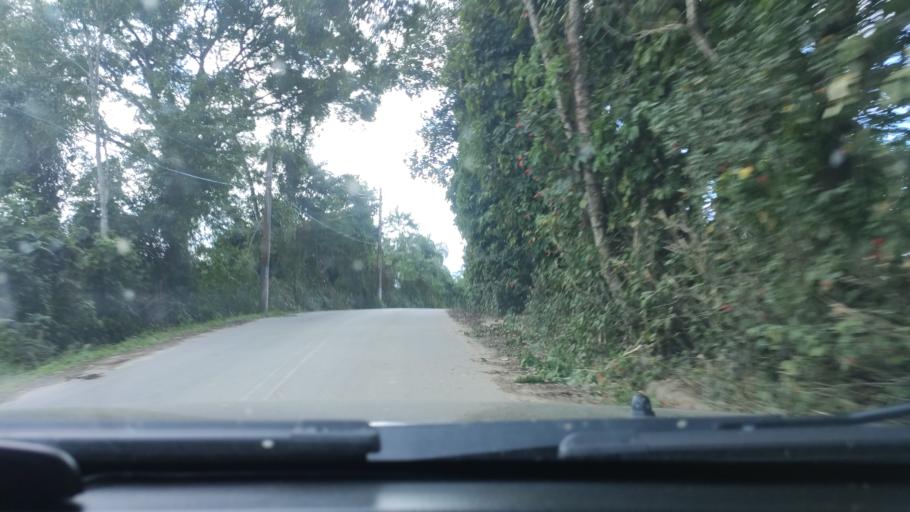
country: BR
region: Sao Paulo
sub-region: Sao Sebastiao
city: Sao Sebastiao
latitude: -23.6994
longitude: -45.4831
